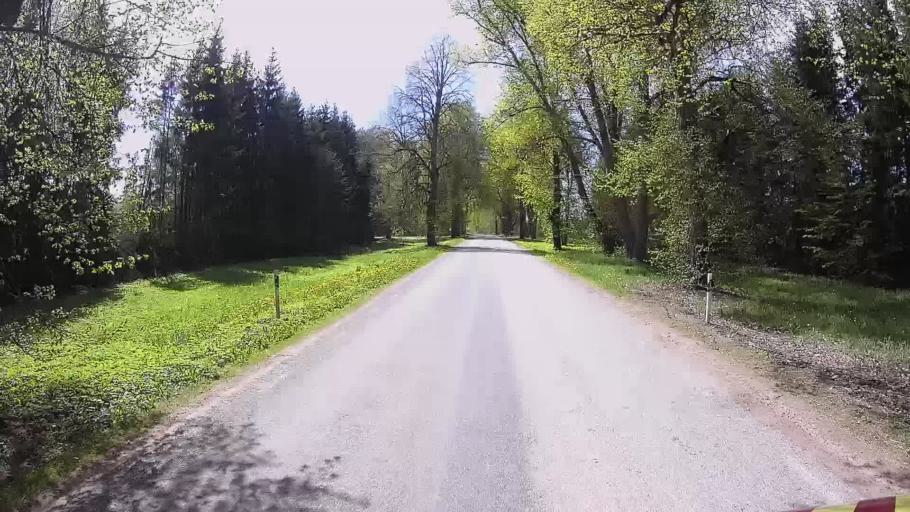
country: LV
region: Apes Novads
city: Ape
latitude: 57.6162
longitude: 26.5859
